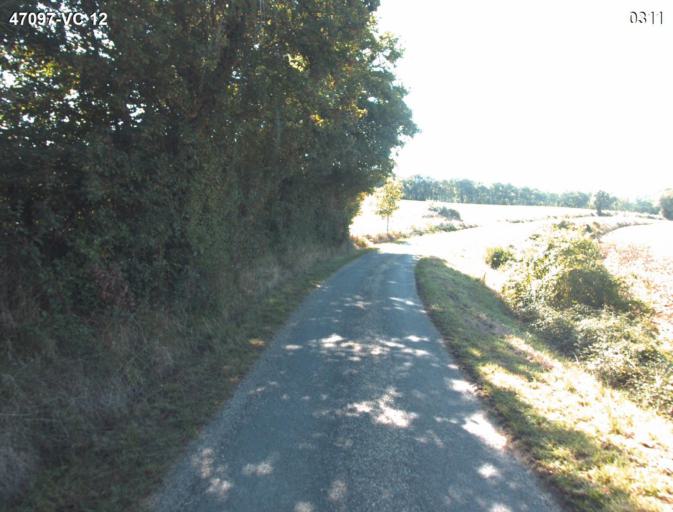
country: FR
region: Aquitaine
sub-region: Departement du Lot-et-Garonne
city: Vianne
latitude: 44.1936
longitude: 0.3601
